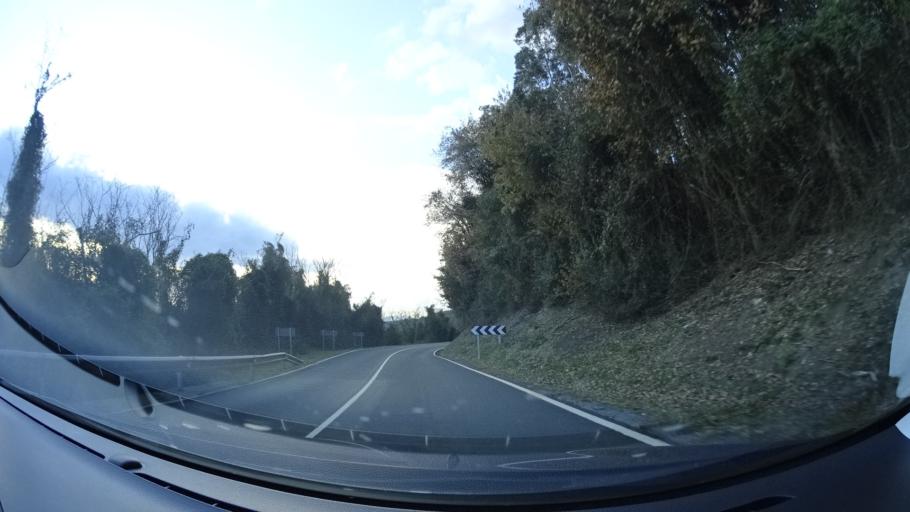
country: ES
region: Basque Country
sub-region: Bizkaia
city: Elexalde
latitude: 43.4000
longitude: -2.9188
